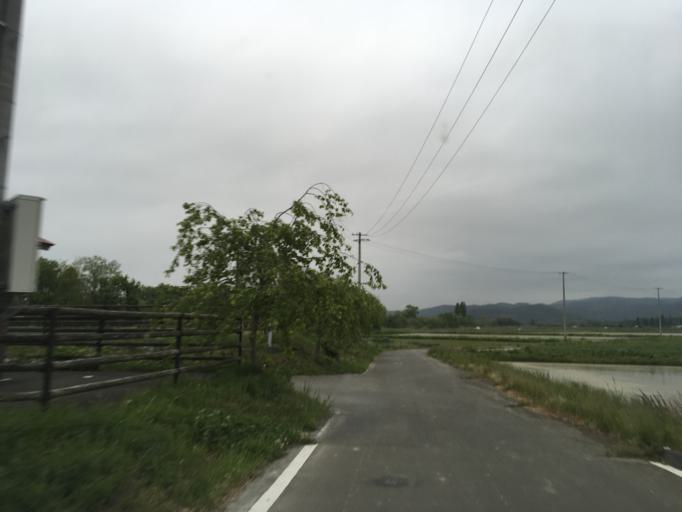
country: JP
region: Miyagi
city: Wakuya
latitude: 38.7098
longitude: 141.2842
